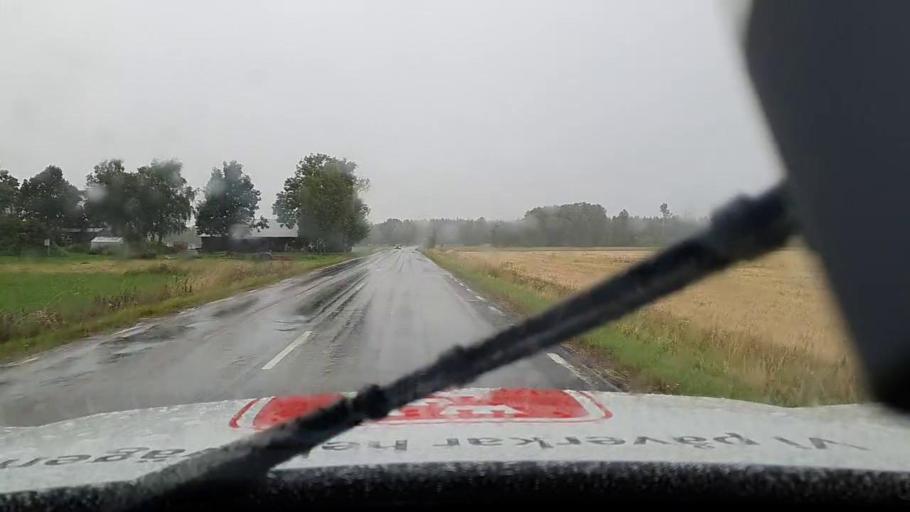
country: SE
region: Vaestra Goetaland
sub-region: Toreboda Kommun
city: Toereboda
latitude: 58.6763
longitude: 14.1336
